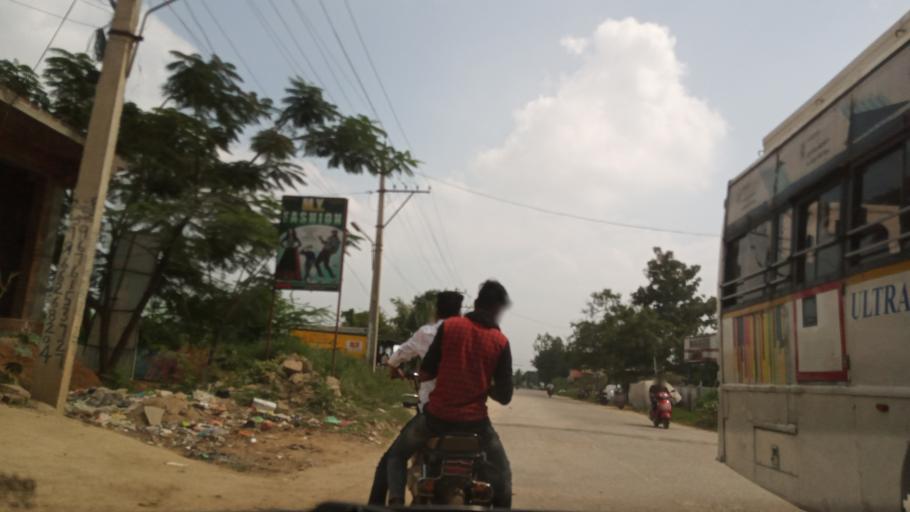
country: IN
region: Andhra Pradesh
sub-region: Chittoor
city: Madanapalle
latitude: 13.6389
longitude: 78.6349
